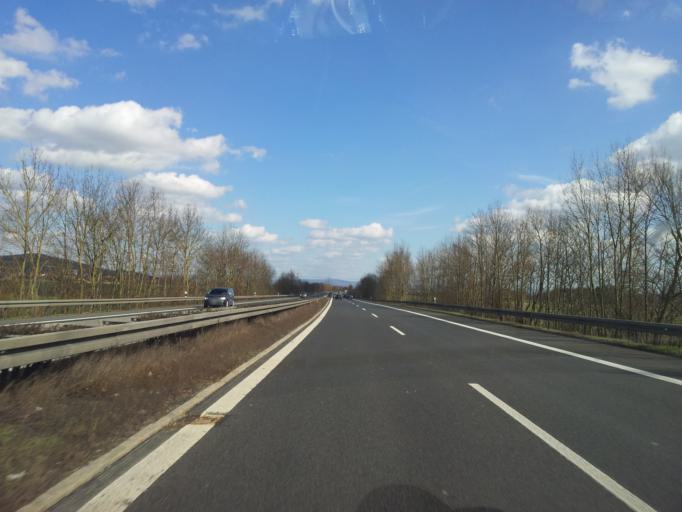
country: DE
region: Bavaria
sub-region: Upper Franconia
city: Viereth-Trunstadt
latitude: 49.9278
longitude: 10.7926
